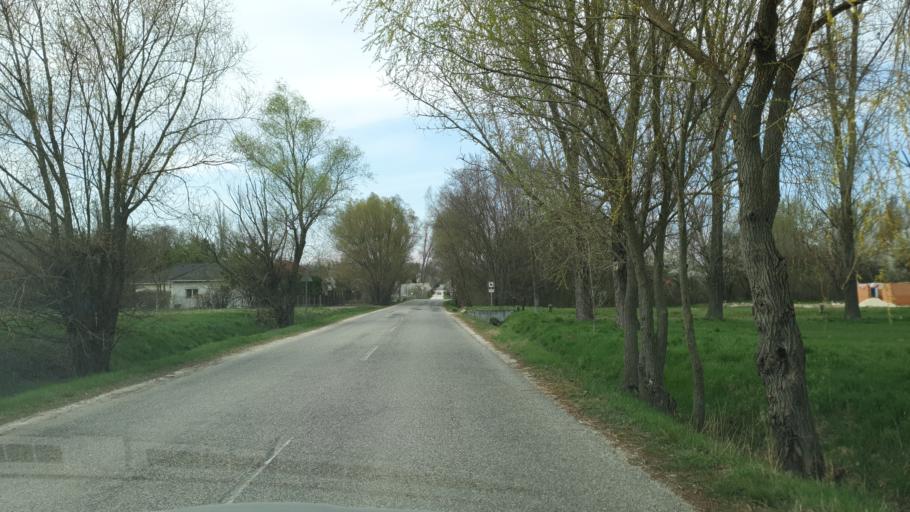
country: HU
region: Fejer
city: Etyek
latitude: 47.4562
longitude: 18.7279
